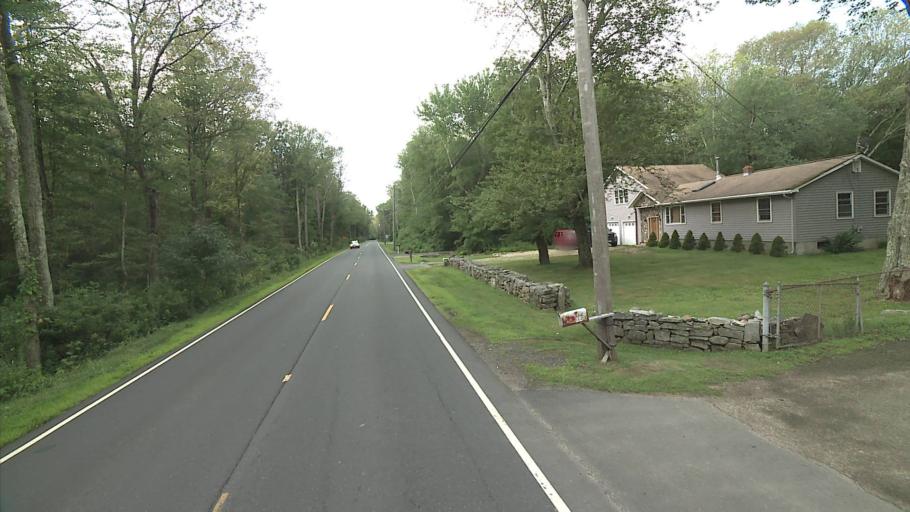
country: US
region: Connecticut
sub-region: Middlesex County
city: Moodus
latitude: 41.5299
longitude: -72.4124
